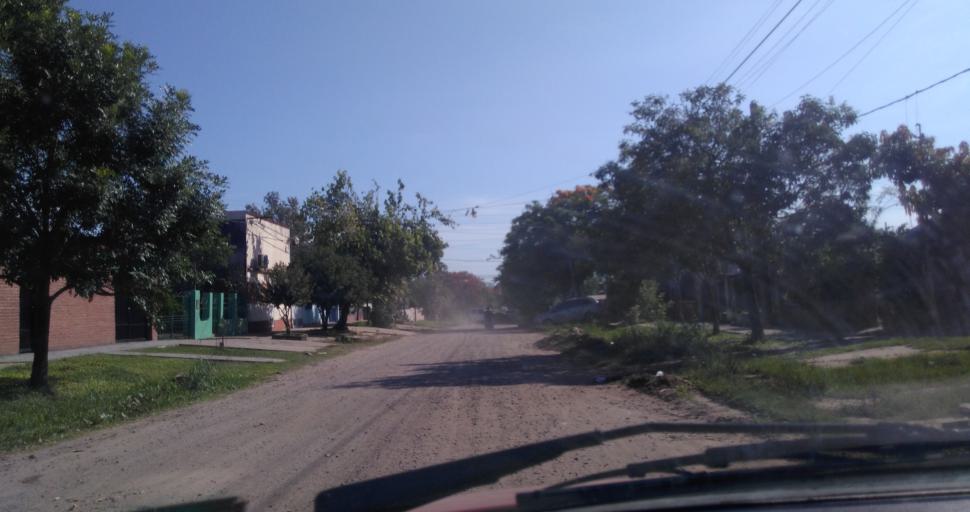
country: AR
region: Chaco
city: Resistencia
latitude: -27.4646
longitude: -58.9673
